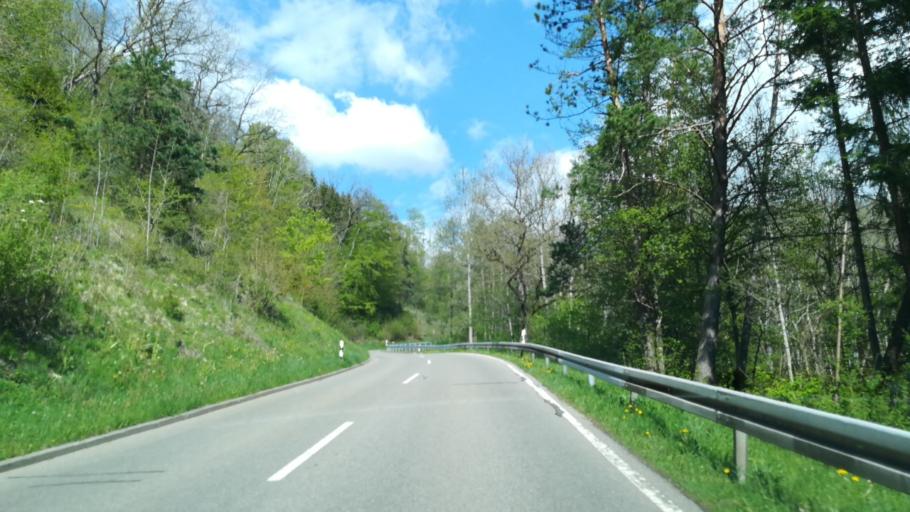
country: DE
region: Baden-Wuerttemberg
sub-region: Freiburg Region
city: Blumberg
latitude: 47.8395
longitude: 8.5181
